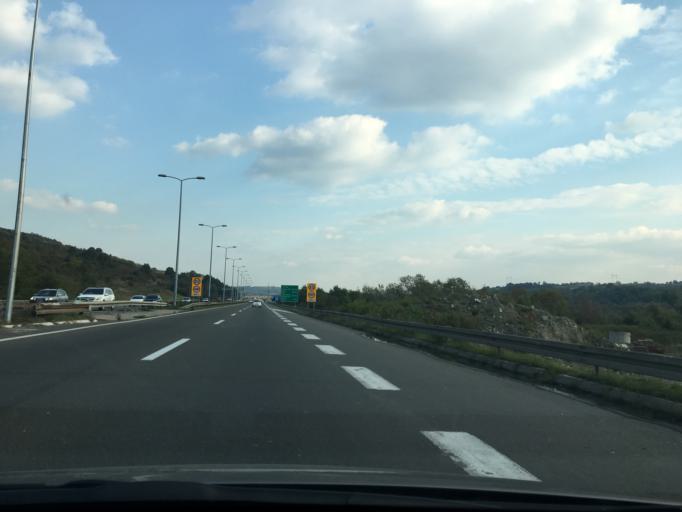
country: RS
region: Central Serbia
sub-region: Belgrade
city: Zvezdara
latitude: 44.7223
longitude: 20.5458
